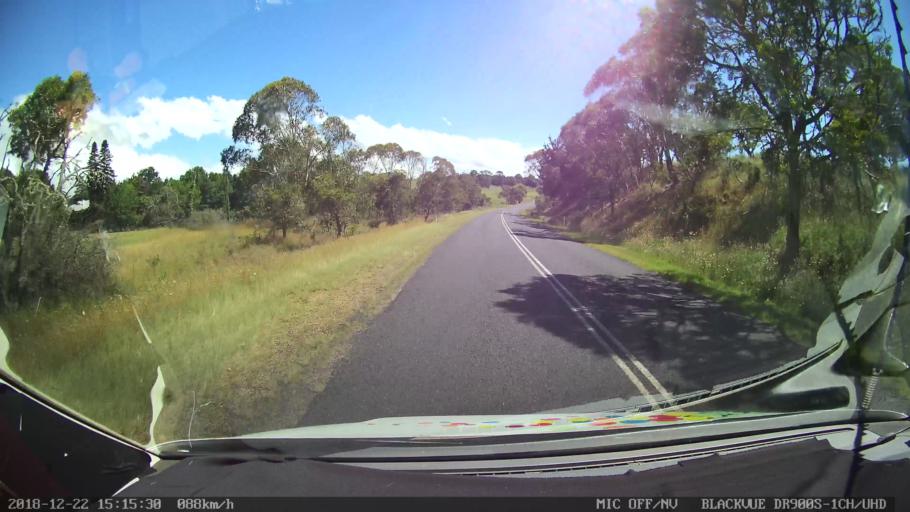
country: AU
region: New South Wales
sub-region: Bellingen
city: Dorrigo
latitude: -30.3798
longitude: 152.3667
